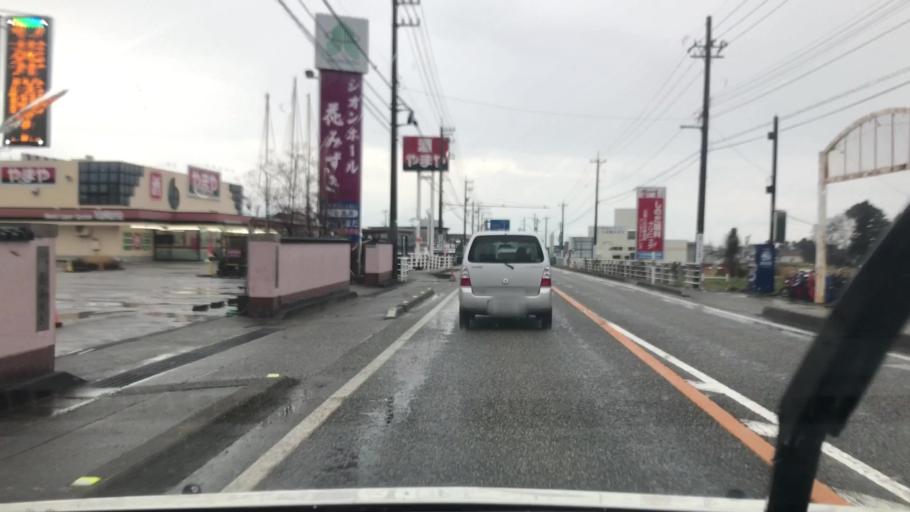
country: JP
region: Toyama
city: Yatsuomachi-higashikumisaka
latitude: 36.5964
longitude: 137.2037
